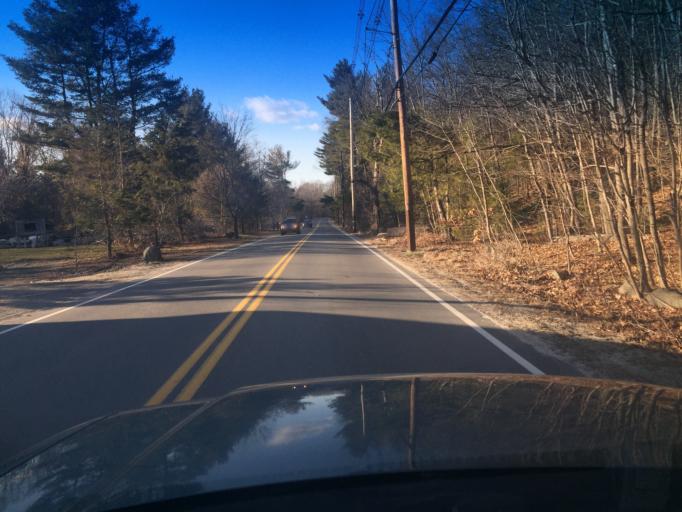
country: US
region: Massachusetts
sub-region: Middlesex County
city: Sherborn
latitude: 42.2584
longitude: -71.3726
